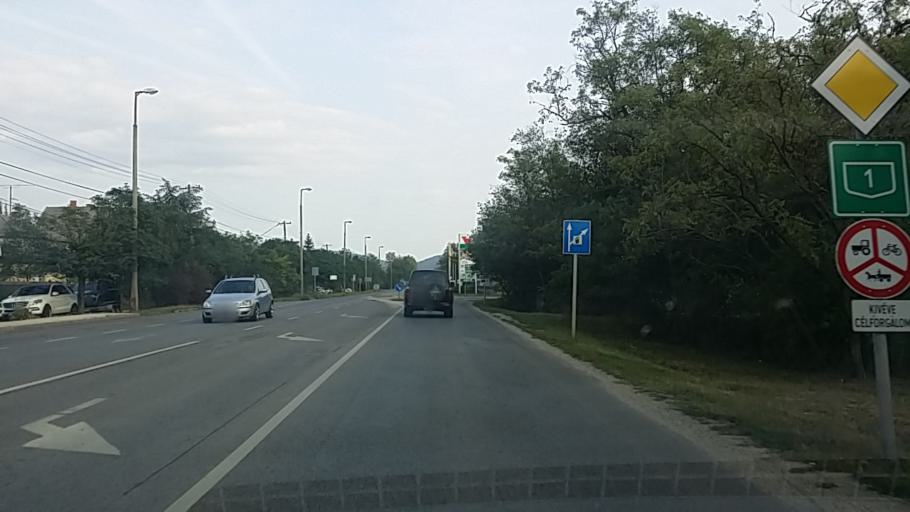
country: HU
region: Komarom-Esztergom
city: Baj
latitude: 47.6388
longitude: 18.3464
